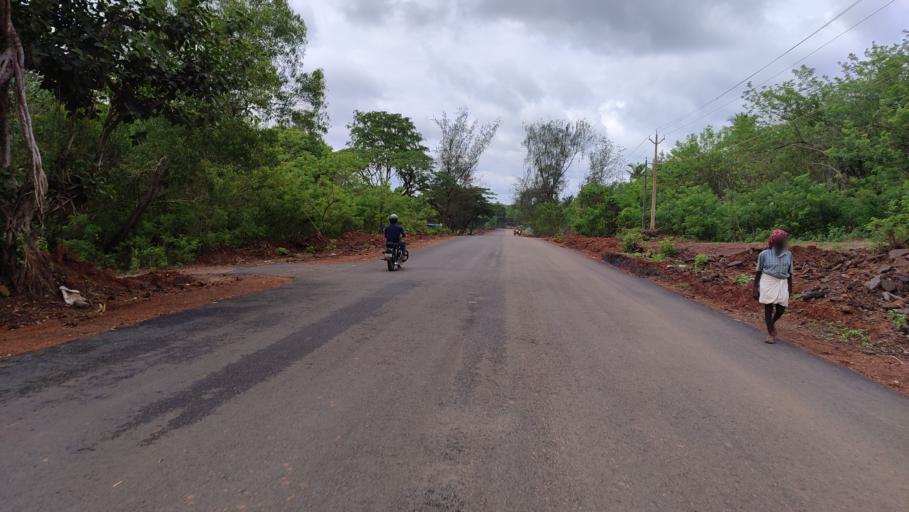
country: IN
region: Kerala
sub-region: Kasaragod District
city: Kasaragod
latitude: 12.5367
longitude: 75.0716
